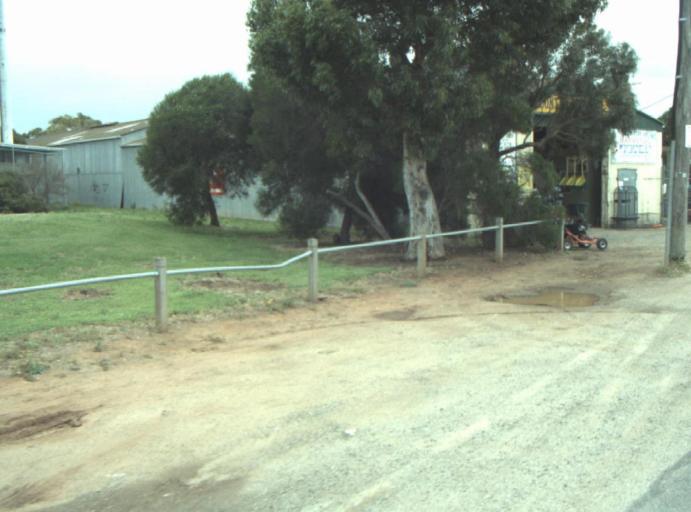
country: AU
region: Victoria
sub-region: Greater Geelong
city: Lara
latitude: -38.0198
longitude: 144.4151
